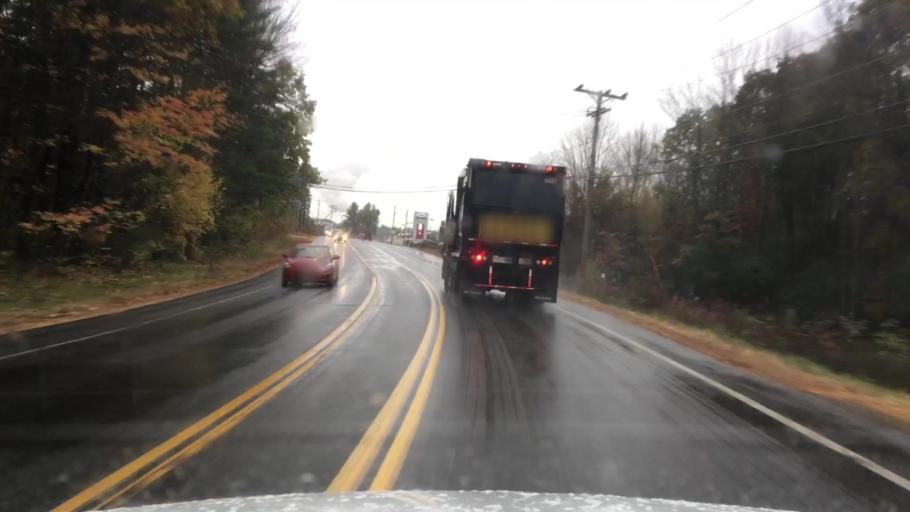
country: US
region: New Hampshire
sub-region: Strafford County
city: Somersworth
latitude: 43.2554
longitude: -70.8991
